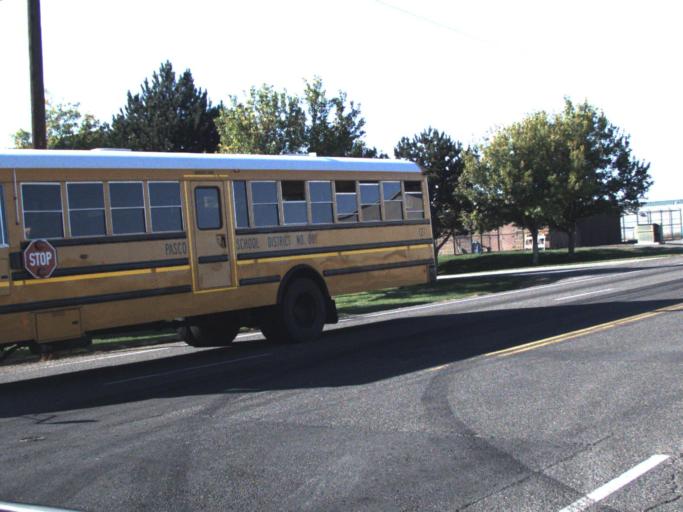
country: US
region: Washington
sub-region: Franklin County
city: Pasco
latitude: 46.2354
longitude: -119.0811
